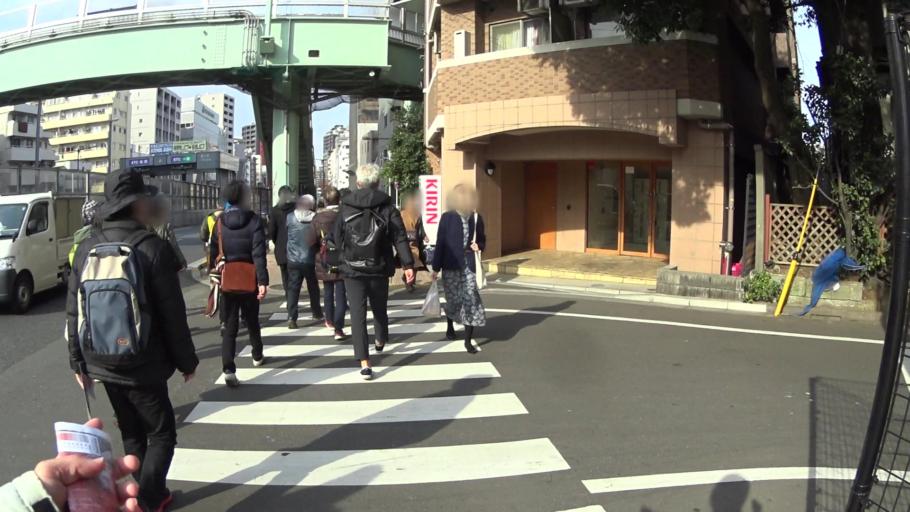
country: JP
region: Tokyo
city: Tokyo
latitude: 35.6626
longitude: 139.6877
